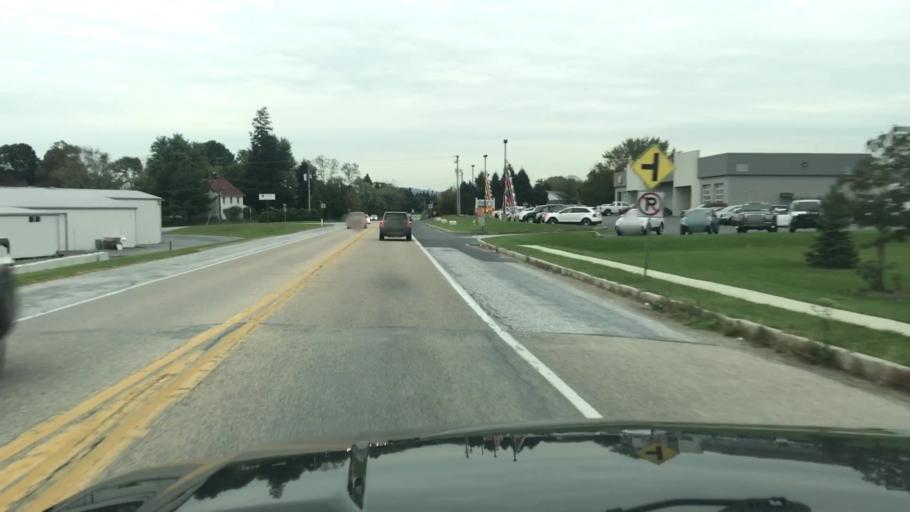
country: US
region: Pennsylvania
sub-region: Cumberland County
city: Mechanicsburg
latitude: 40.1754
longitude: -76.9840
